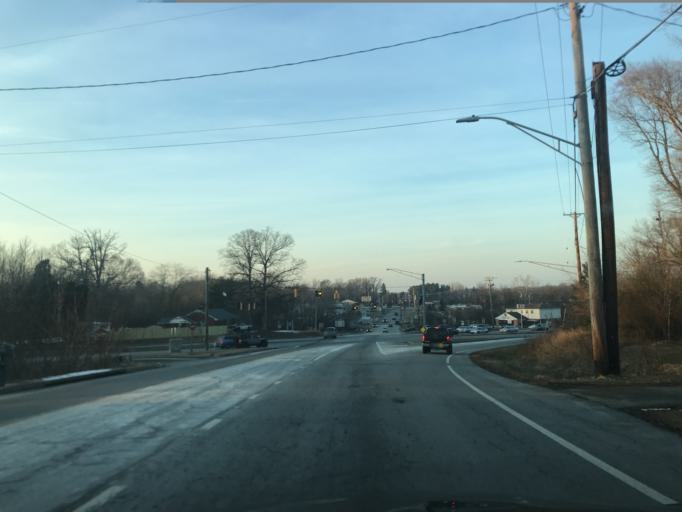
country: US
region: Maryland
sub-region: Harford County
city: Edgewood
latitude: 39.4320
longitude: -76.3053
